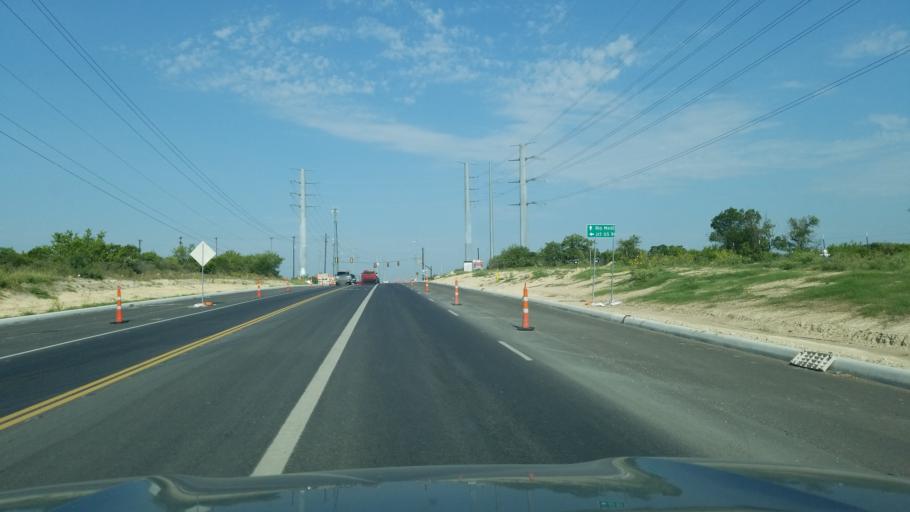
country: US
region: Texas
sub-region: Medina County
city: La Coste
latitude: 29.4214
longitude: -98.7805
